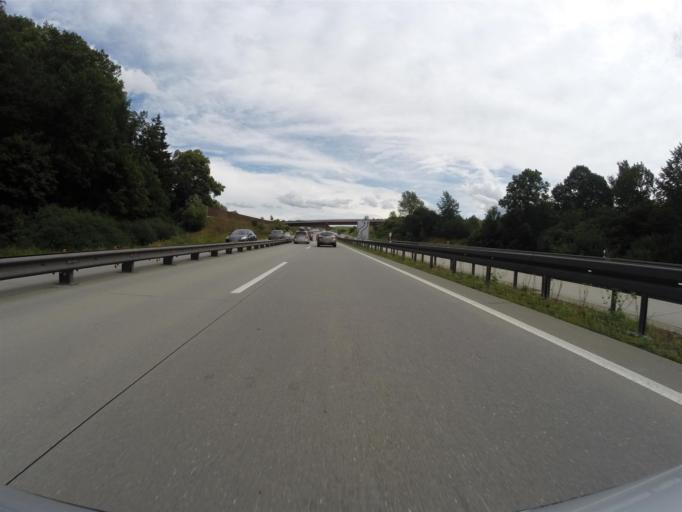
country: DE
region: Thuringia
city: Gorkwitz
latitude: 50.5676
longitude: 11.7785
